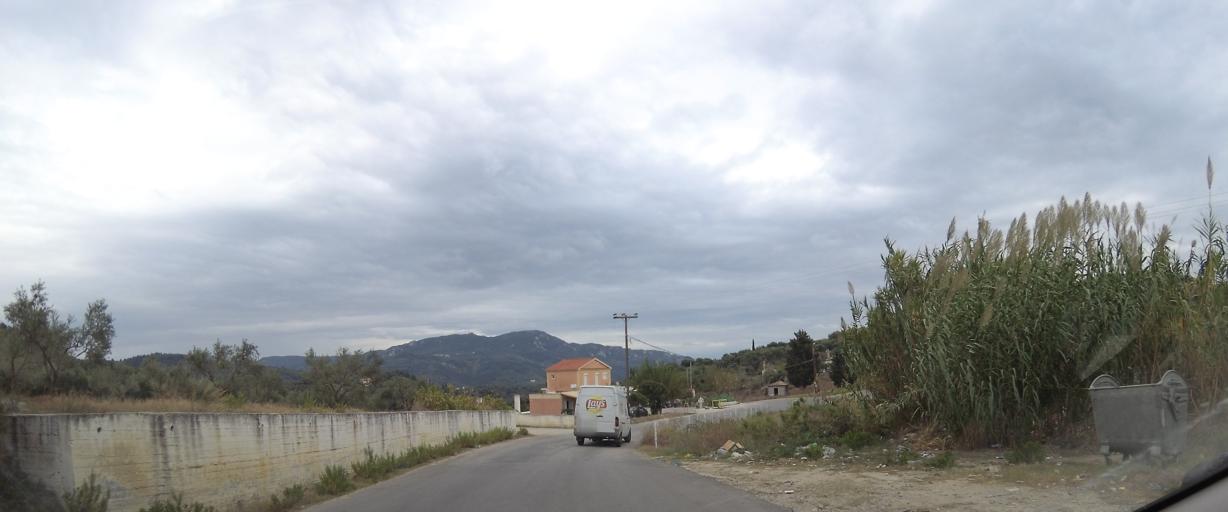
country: GR
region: Ionian Islands
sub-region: Nomos Kerkyras
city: Agios Georgis
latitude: 39.7384
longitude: 19.6743
